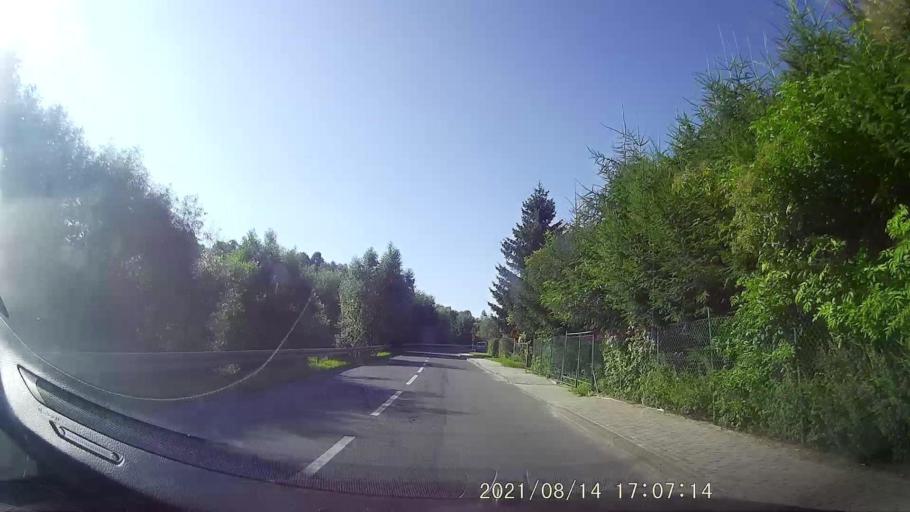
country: PL
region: Lower Silesian Voivodeship
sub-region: Powiat jeleniogorski
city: Kowary
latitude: 50.8158
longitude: 15.8095
